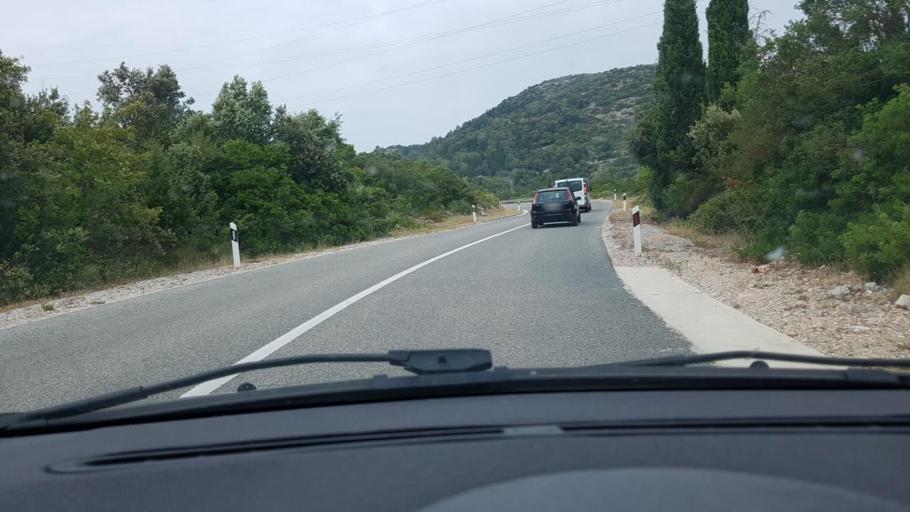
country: HR
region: Dubrovacko-Neretvanska
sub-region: Grad Korcula
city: Zrnovo
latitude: 42.9453
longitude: 17.0465
